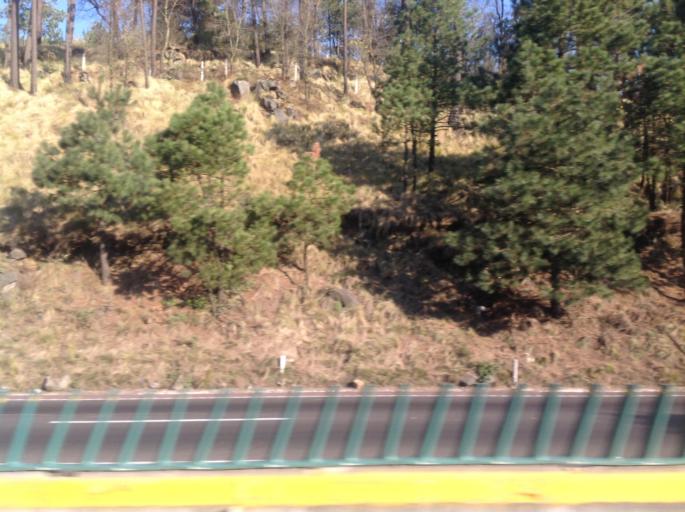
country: MX
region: Mexico
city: Rio Frio de Juarez
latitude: 19.3230
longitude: -98.7245
